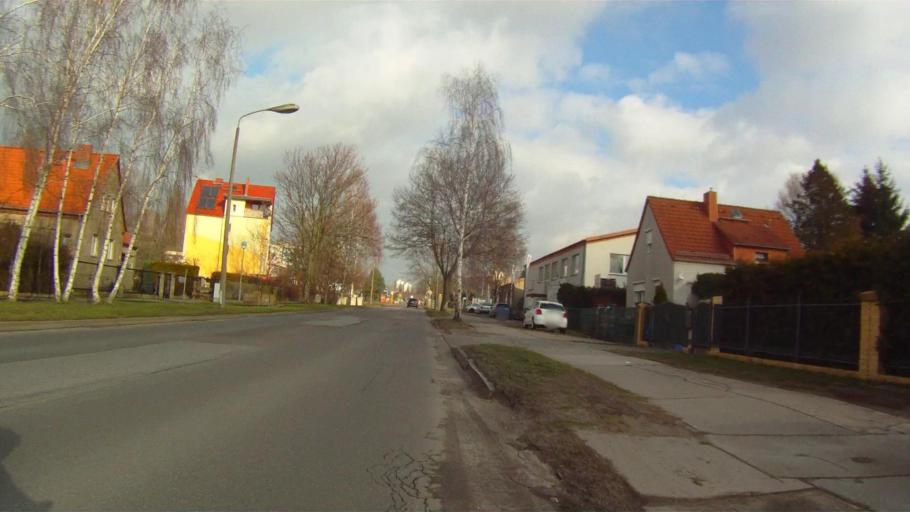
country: DE
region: Berlin
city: Biesdorf
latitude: 52.5209
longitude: 13.5320
